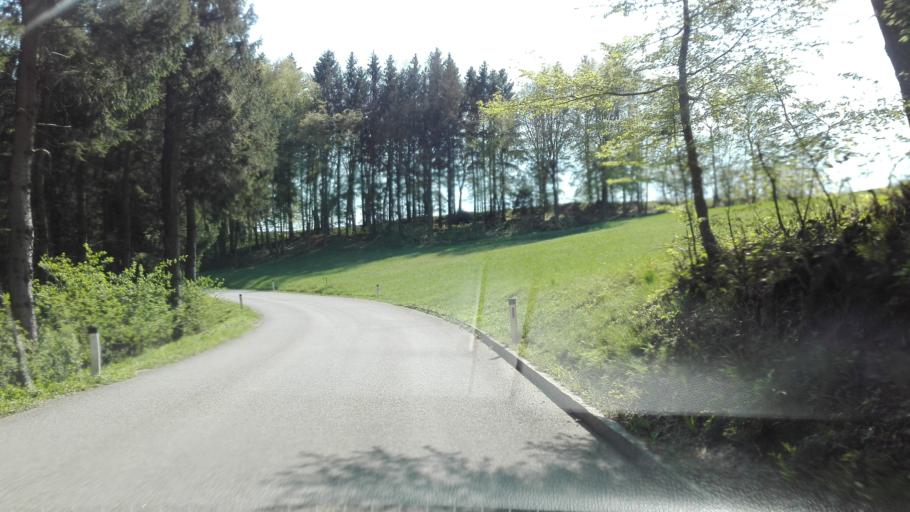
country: AT
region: Upper Austria
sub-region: Politischer Bezirk Rohrbach
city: Atzesberg
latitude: 48.4206
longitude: 13.9175
